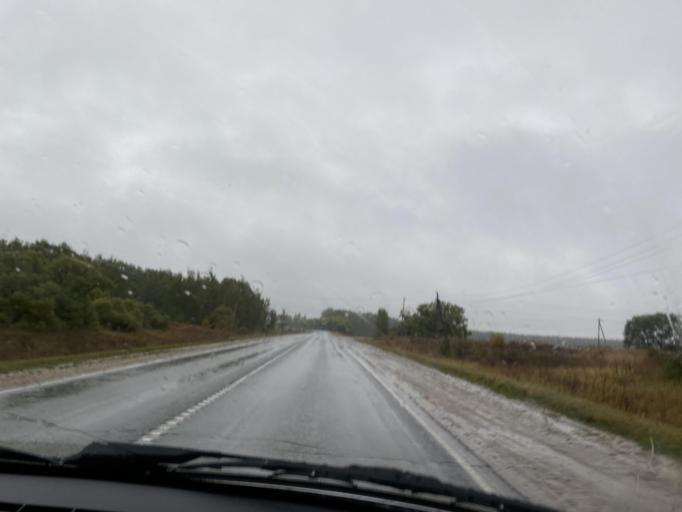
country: RU
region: Rjazan
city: Starozhilovo
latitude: 54.3849
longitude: 39.9254
